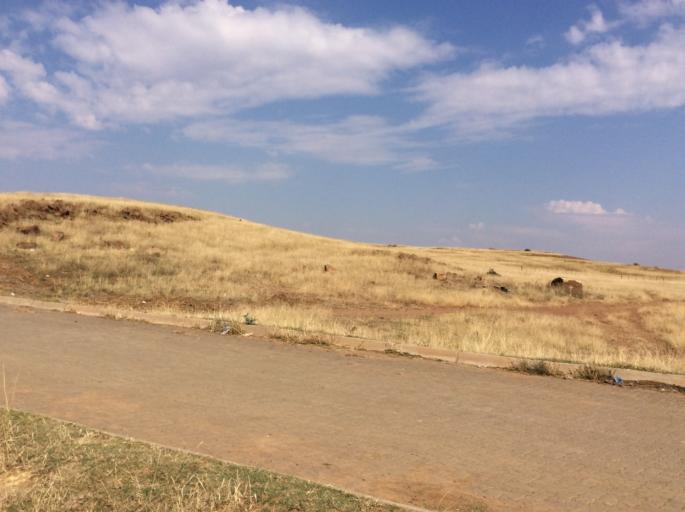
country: LS
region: Mafeteng
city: Mafeteng
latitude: -29.9843
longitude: 27.0047
